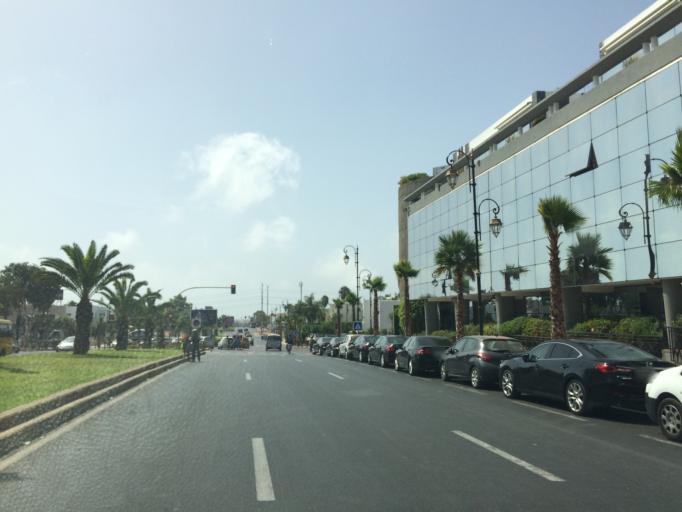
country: MA
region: Rabat-Sale-Zemmour-Zaer
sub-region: Skhirate-Temara
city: Temara
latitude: 33.9598
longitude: -6.8727
